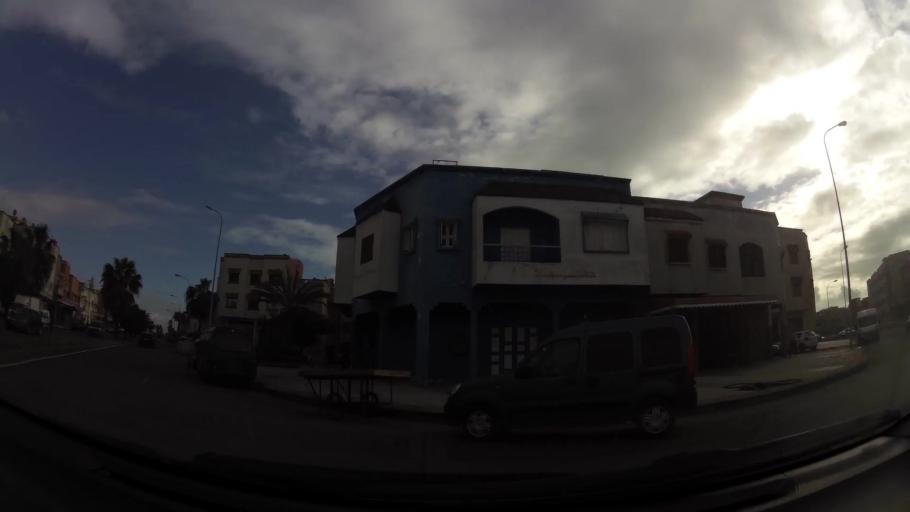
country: MA
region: Doukkala-Abda
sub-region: El-Jadida
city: El Jadida
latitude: 33.2549
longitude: -8.5187
